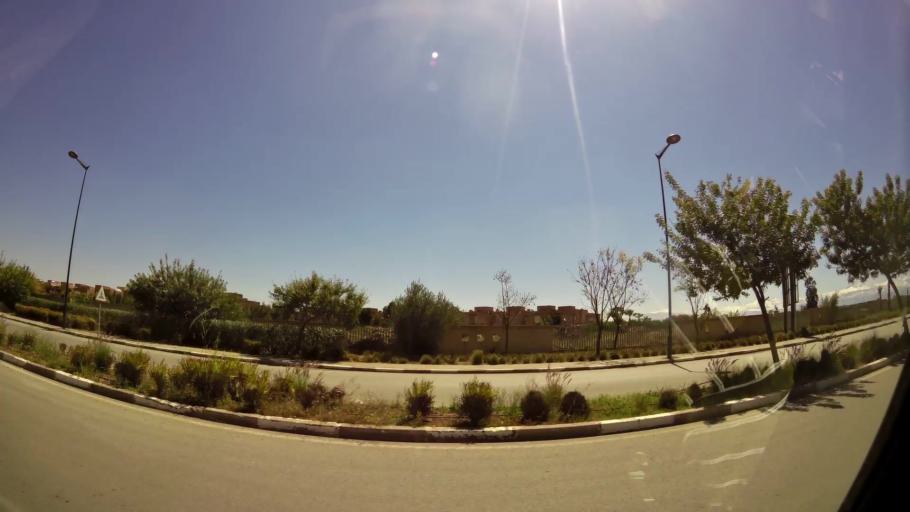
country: MA
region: Marrakech-Tensift-Al Haouz
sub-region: Marrakech
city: Marrakesh
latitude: 31.5990
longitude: -8.0059
